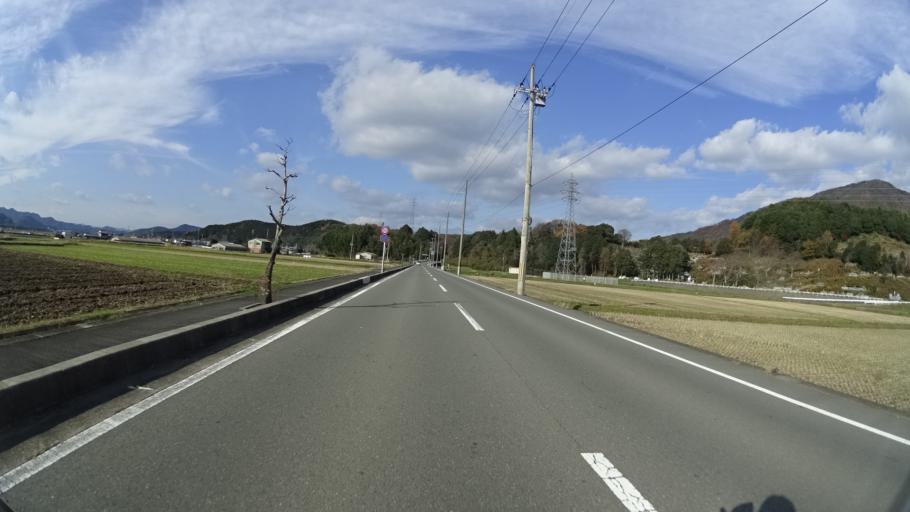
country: JP
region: Kyoto
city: Kameoka
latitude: 35.0608
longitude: 135.5677
